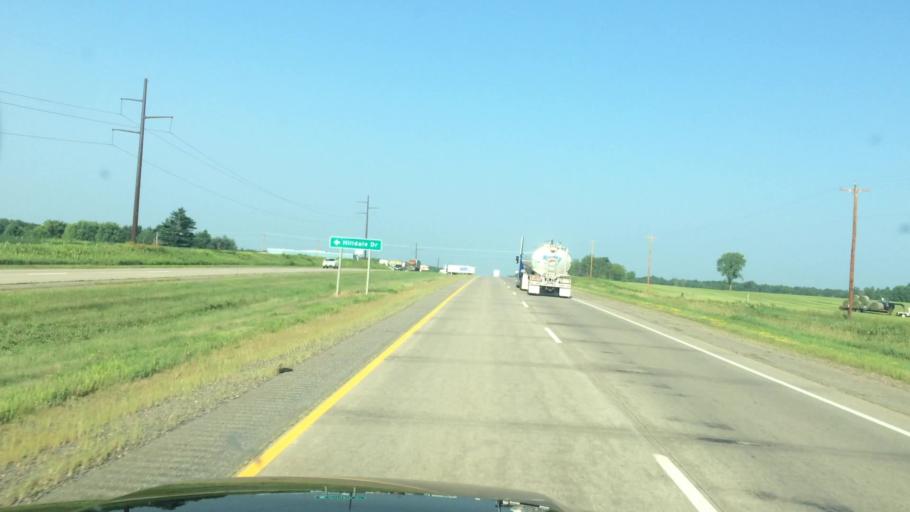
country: US
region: Wisconsin
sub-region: Marathon County
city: Edgar
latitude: 44.9444
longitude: -89.9999
